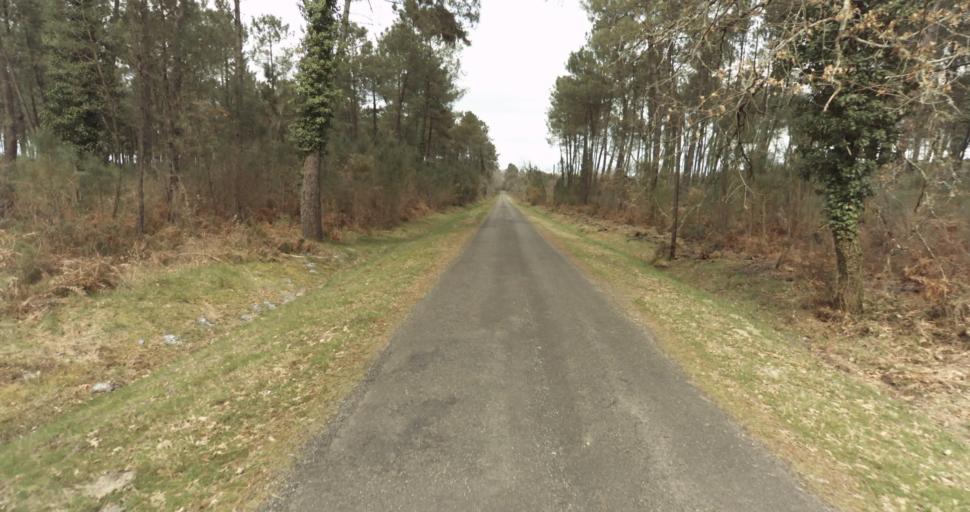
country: FR
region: Aquitaine
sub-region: Departement des Landes
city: Roquefort
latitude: 44.0549
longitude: -0.3779
